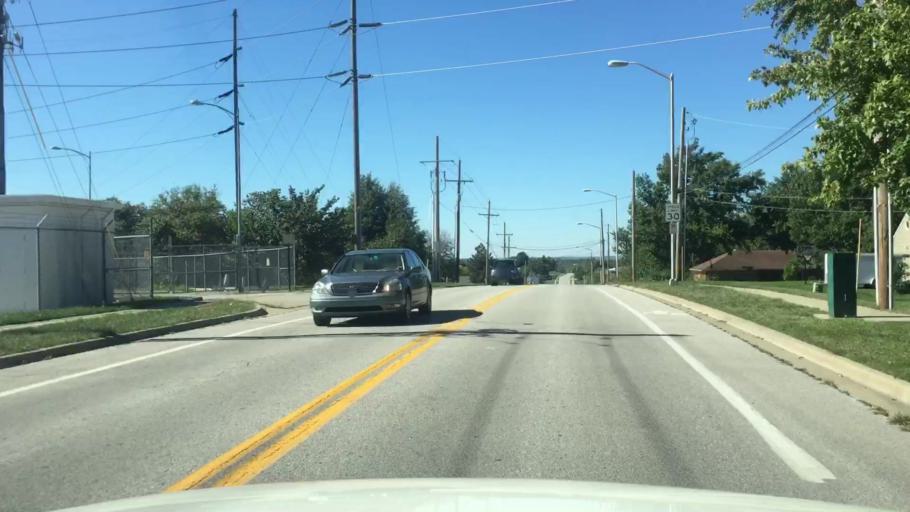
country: US
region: Kansas
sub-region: Johnson County
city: Shawnee
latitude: 39.0366
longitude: -94.7316
